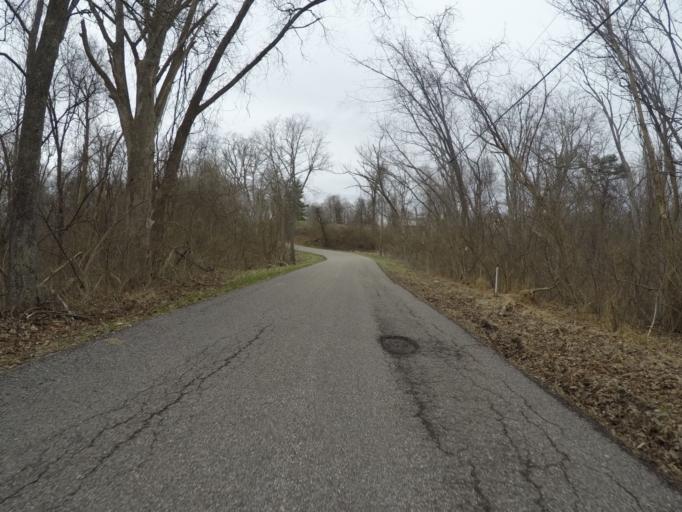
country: US
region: West Virginia
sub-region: Wayne County
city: Lavalette
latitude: 38.3694
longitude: -82.4276
